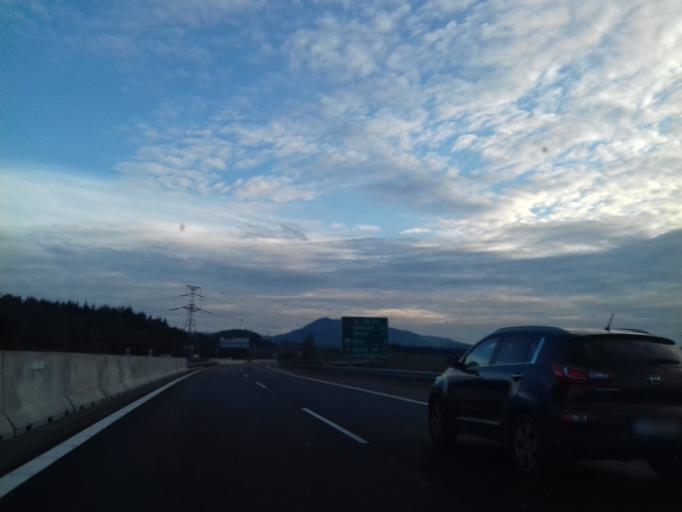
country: SK
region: Trenciansky
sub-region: Okres Povazska Bystrica
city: Povazska Bystrica
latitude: 49.0900
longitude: 18.4192
